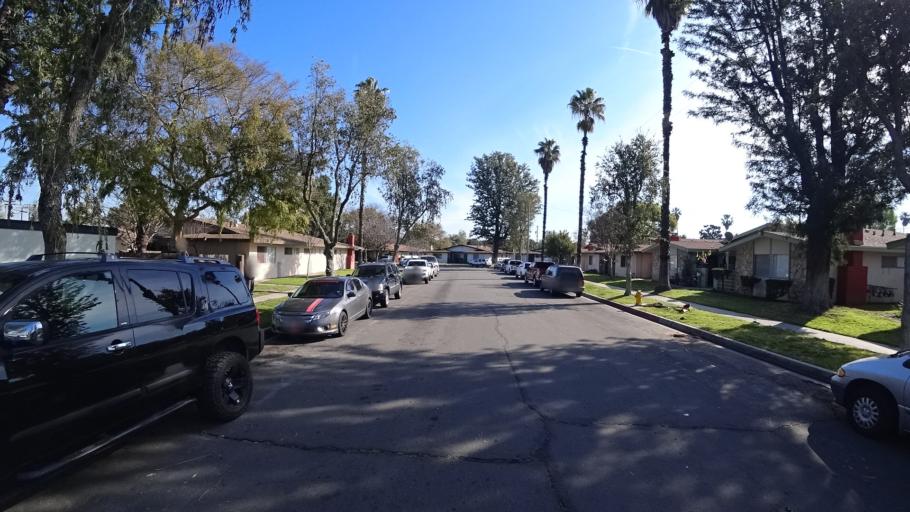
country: US
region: California
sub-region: Orange County
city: Fullerton
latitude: 33.8497
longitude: -117.9340
